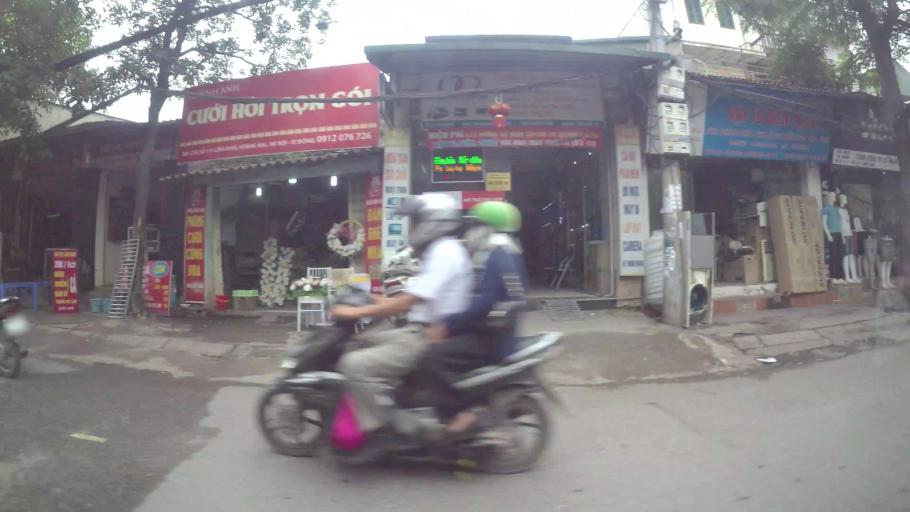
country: VN
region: Ha Noi
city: Hai BaTrung
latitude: 20.9865
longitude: 105.8691
